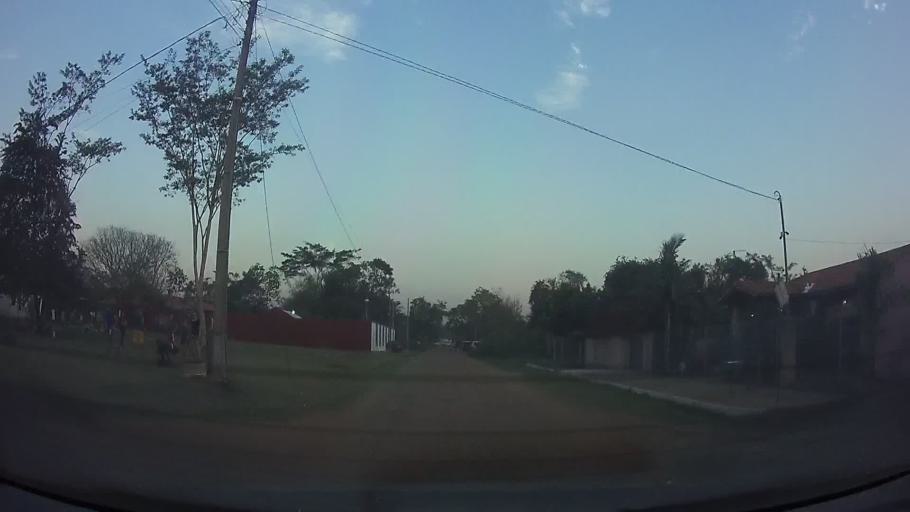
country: PY
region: Central
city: Limpio
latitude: -25.2313
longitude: -57.4696
